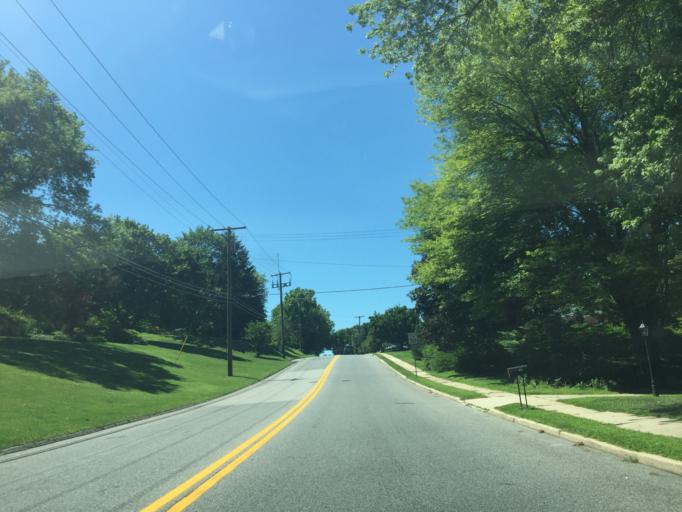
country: US
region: Maryland
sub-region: Baltimore County
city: Timonium
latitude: 39.4535
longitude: -76.6054
